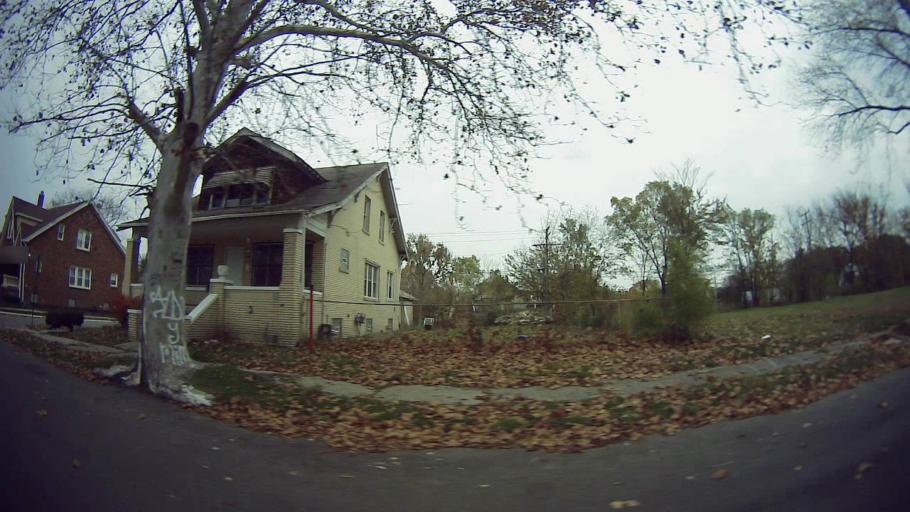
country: US
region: Michigan
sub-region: Wayne County
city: Hamtramck
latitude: 42.4062
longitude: -83.0673
